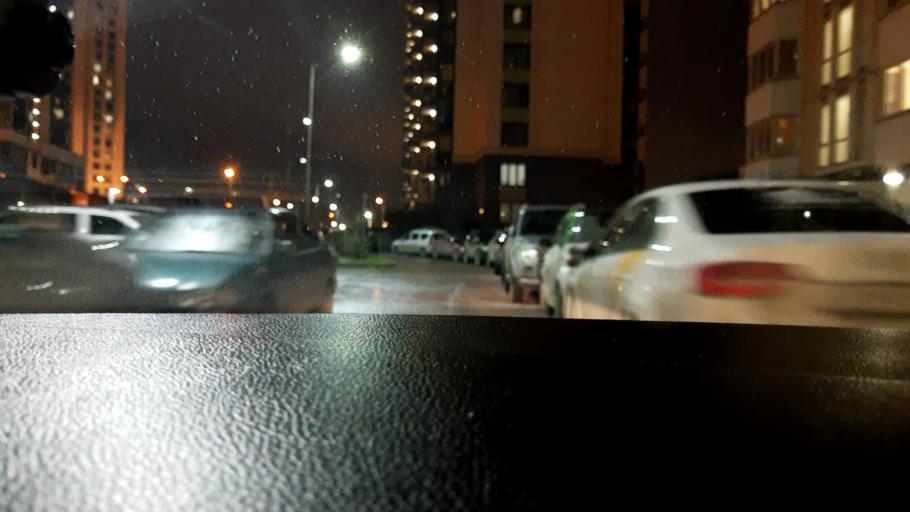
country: RU
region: Moscow
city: Novo-Peredelkino
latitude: 55.6342
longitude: 37.3204
